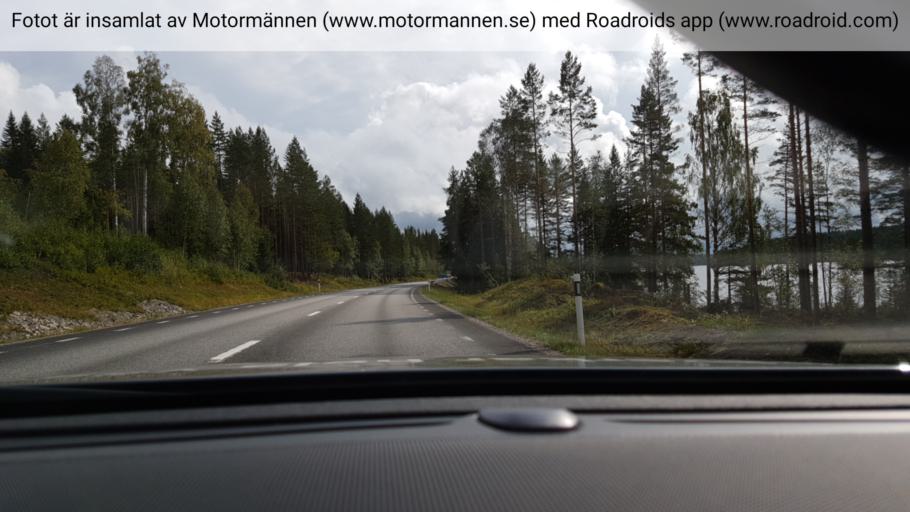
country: SE
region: Dalarna
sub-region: Faluns Kommun
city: Bjursas
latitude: 60.7769
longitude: 15.3158
